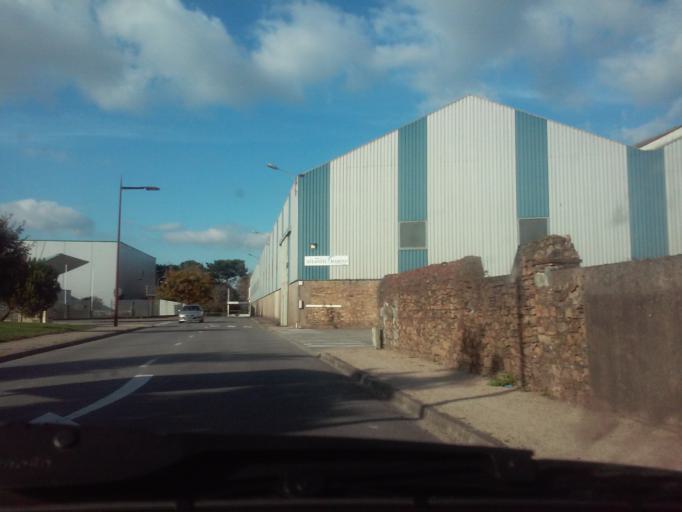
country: FR
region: Pays de la Loire
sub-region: Departement de la Loire-Atlantique
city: Saint-Paimboeuf
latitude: 47.2843
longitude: -2.0164
